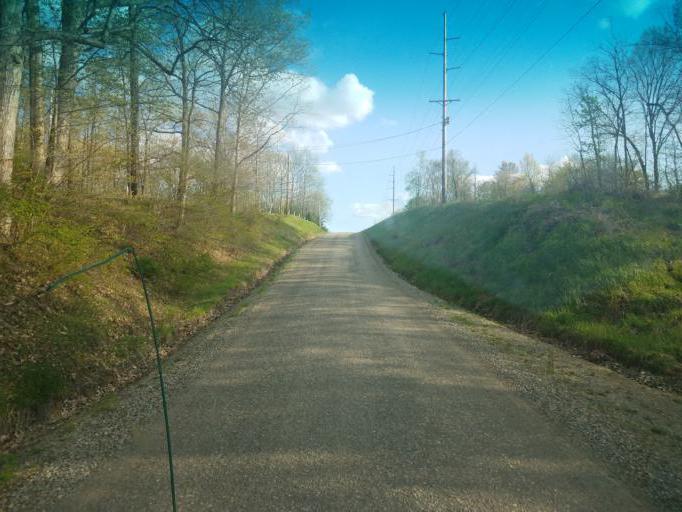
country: US
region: Ohio
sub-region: Wayne County
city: Shreve
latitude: 40.6487
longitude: -82.0335
